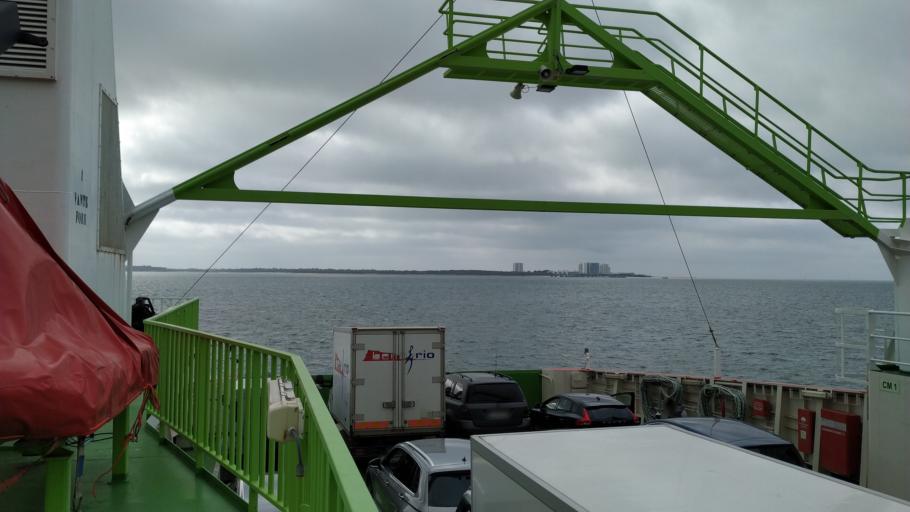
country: PT
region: Setubal
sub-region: Setubal
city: Setubal
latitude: 38.5173
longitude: -8.8858
